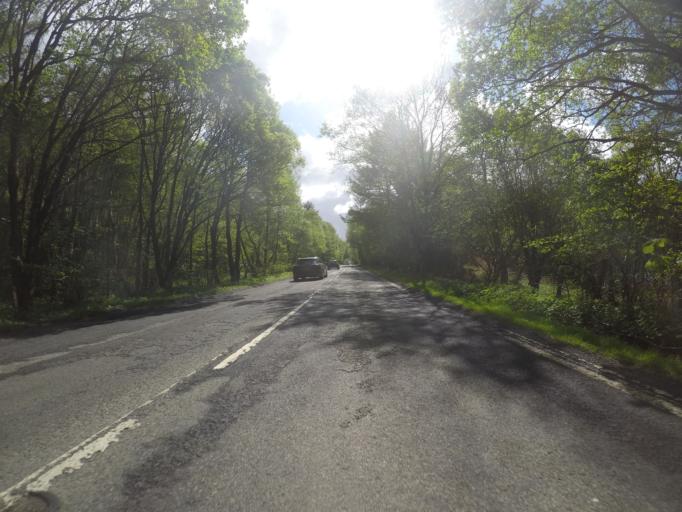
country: GB
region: Scotland
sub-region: Highland
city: Fort William
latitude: 57.2499
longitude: -5.4717
